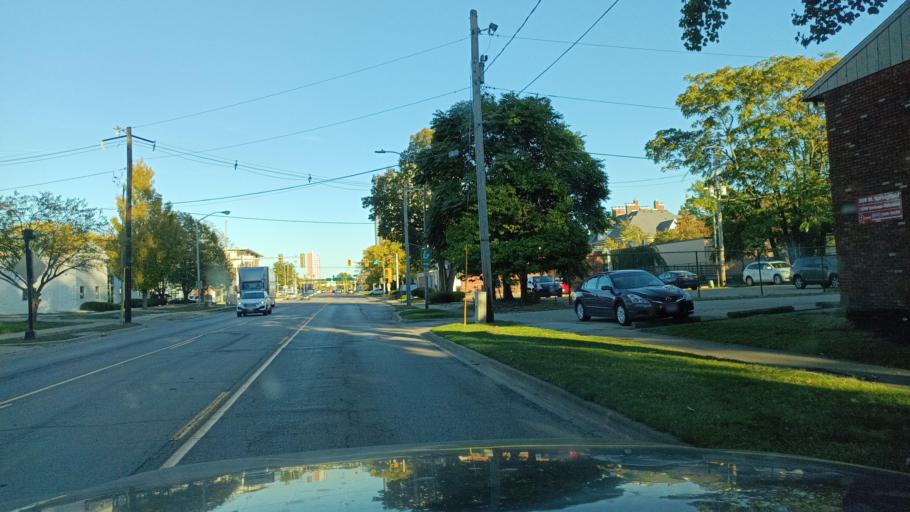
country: US
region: Illinois
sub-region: Champaign County
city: Champaign
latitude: 40.1126
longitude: -88.2482
